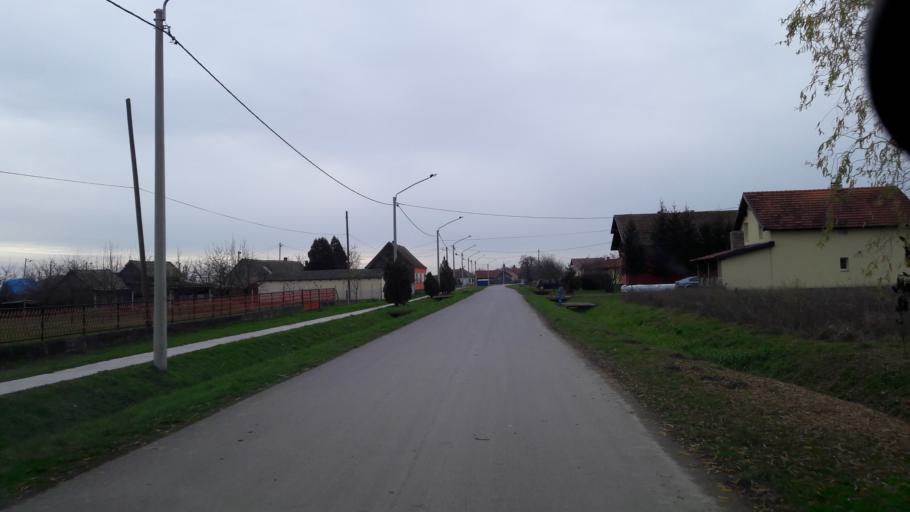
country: HR
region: Osjecko-Baranjska
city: Vladislavci
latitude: 45.4577
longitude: 18.5563
